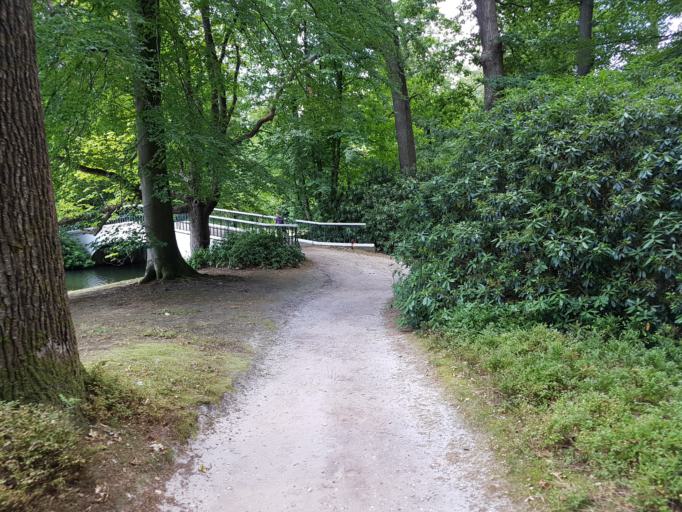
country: NL
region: Gelderland
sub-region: Gemeente Apeldoorn
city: Apeldoorn
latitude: 52.2418
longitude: 5.9482
